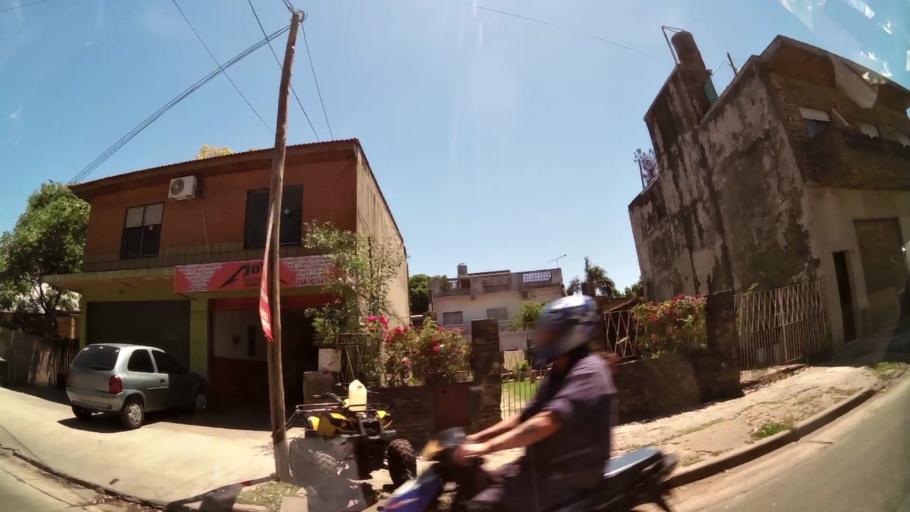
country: AR
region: Buenos Aires
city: Hurlingham
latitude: -34.5080
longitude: -58.7016
